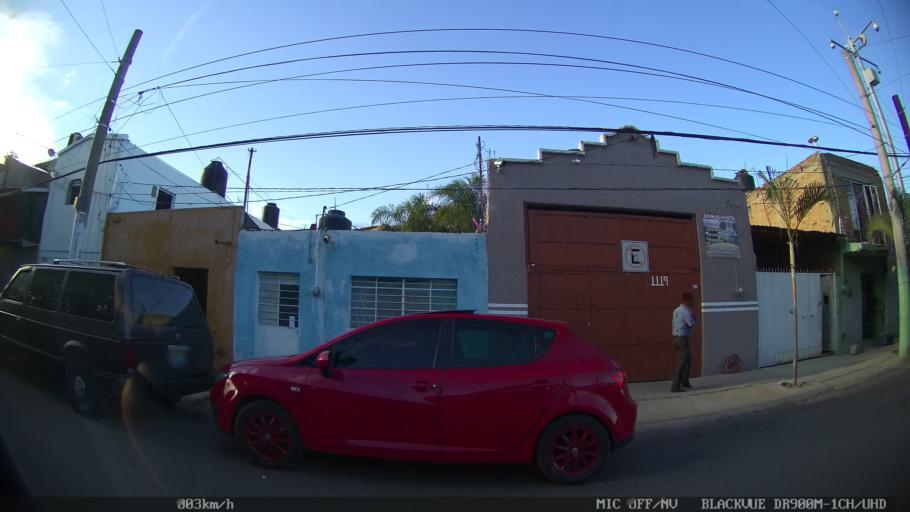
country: MX
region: Jalisco
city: Tlaquepaque
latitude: 20.7084
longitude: -103.3022
